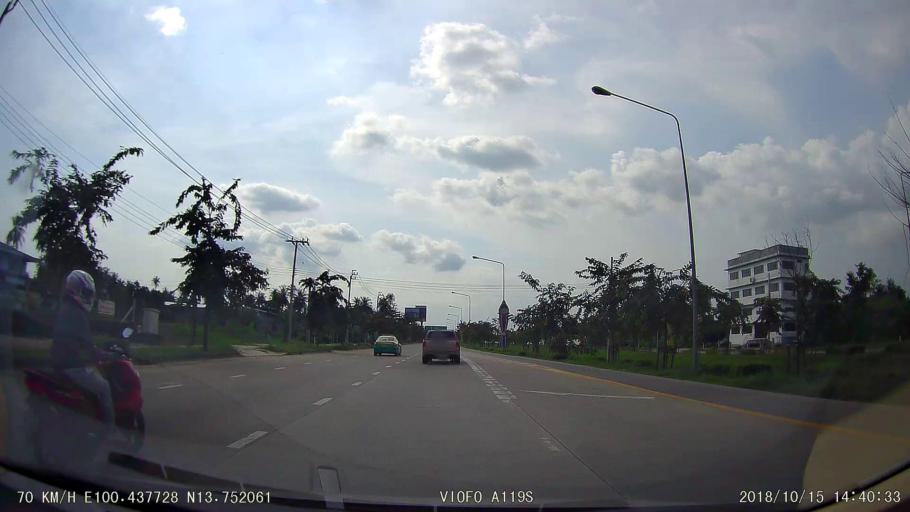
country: TH
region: Bangkok
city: Taling Chan
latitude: 13.7520
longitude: 100.4374
